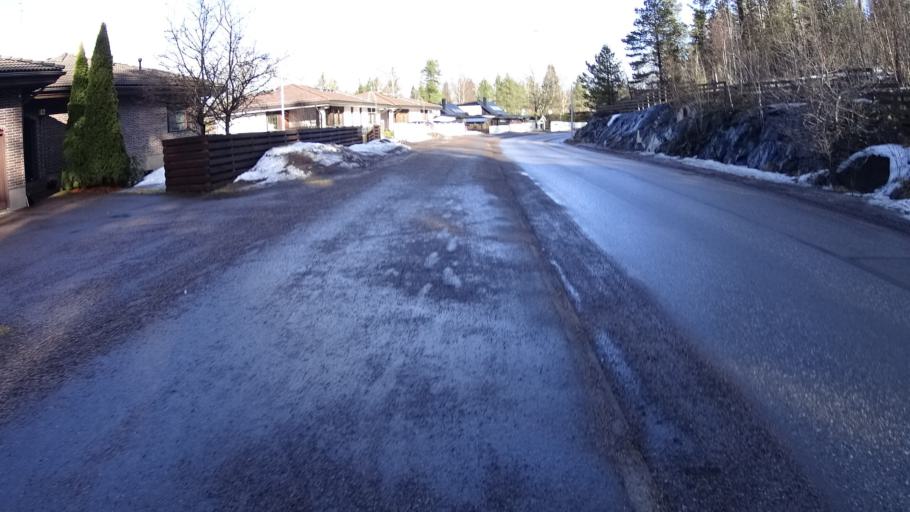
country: FI
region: Uusimaa
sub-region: Helsinki
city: Kilo
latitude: 60.2434
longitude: 24.7596
